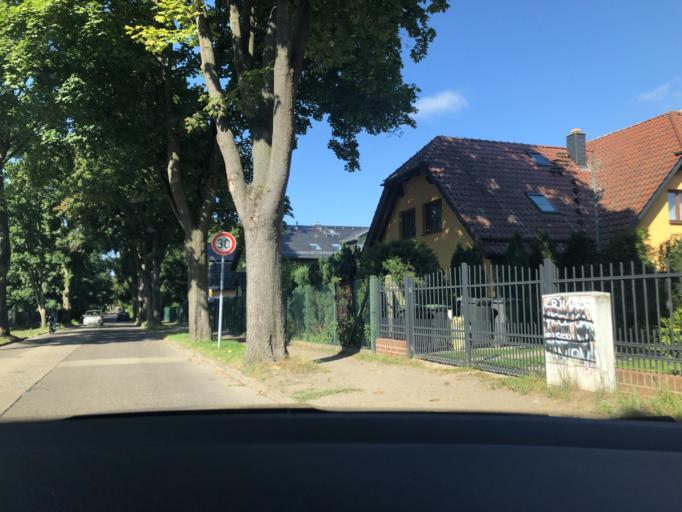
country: DE
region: Brandenburg
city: Erkner
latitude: 52.4149
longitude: 13.7482
